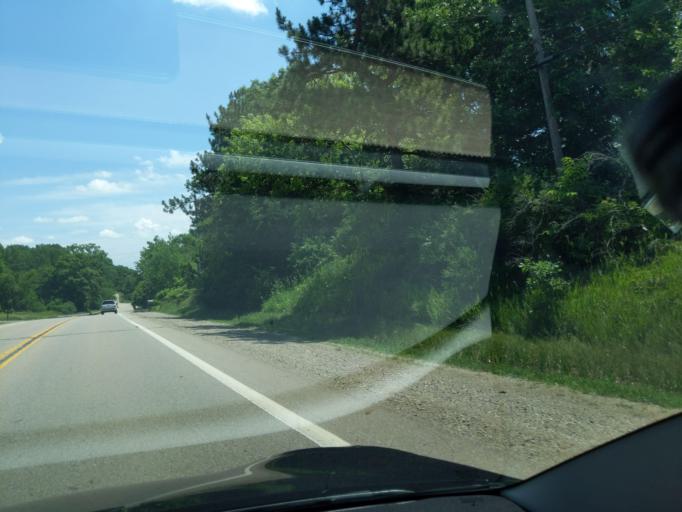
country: US
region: Michigan
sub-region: Ionia County
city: Portland
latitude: 43.0020
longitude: -84.9293
